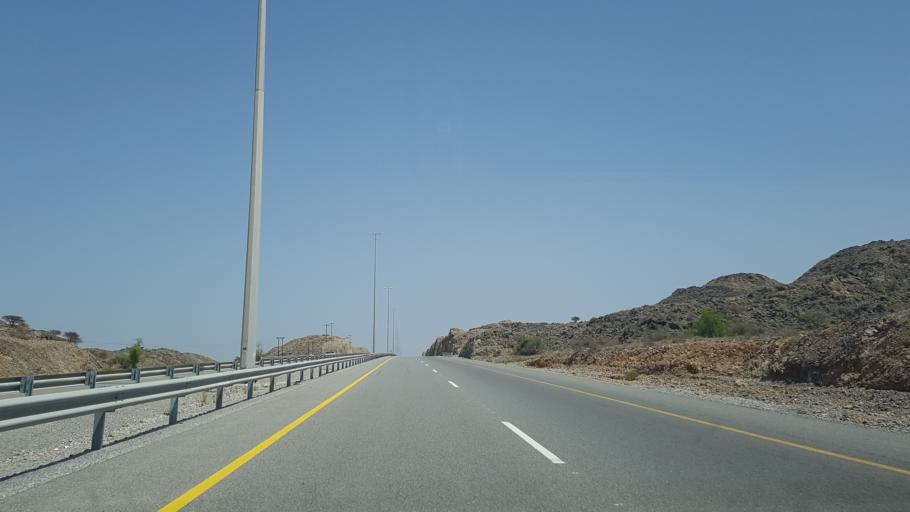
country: OM
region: Muhafazat Masqat
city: Muscat
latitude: 23.2059
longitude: 58.8127
